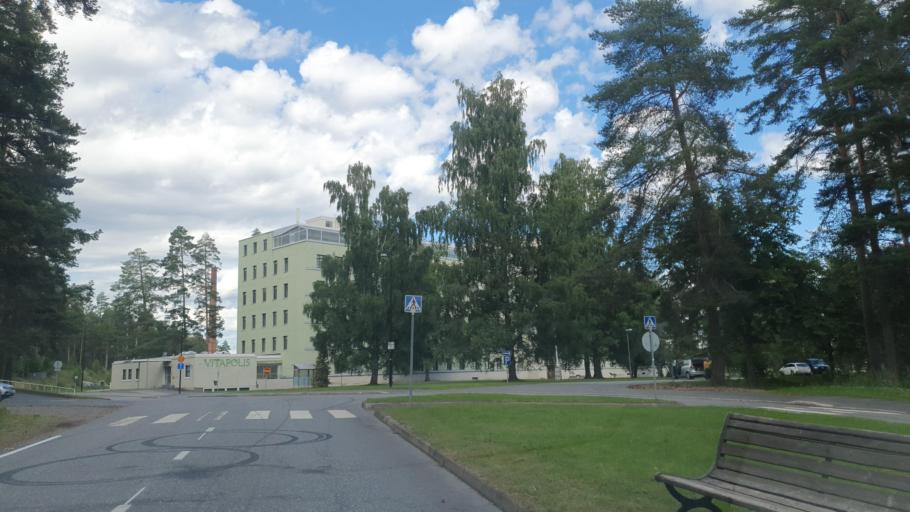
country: FI
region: Central Finland
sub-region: Jyvaeskylae
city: Saeynaetsalo
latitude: 62.1576
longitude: 25.7637
